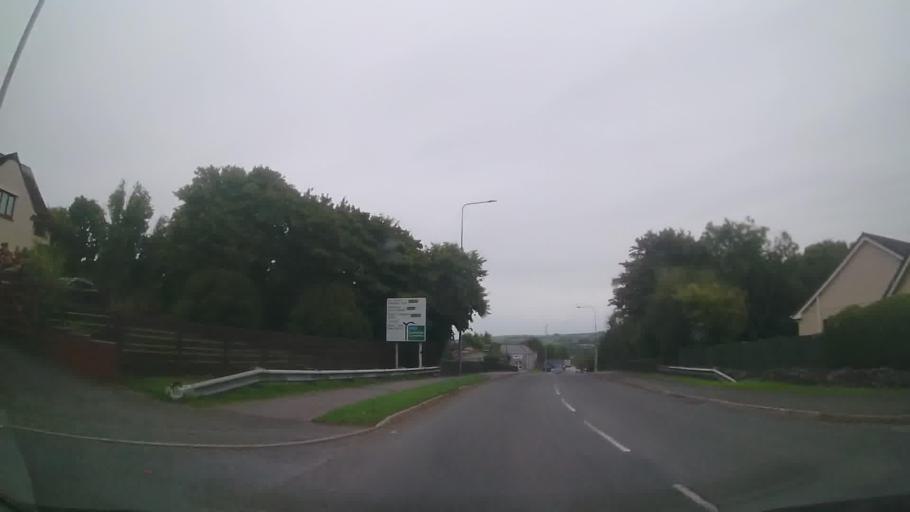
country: GB
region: Wales
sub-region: Carmarthenshire
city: Saint Clears
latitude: 51.8169
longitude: -4.4982
